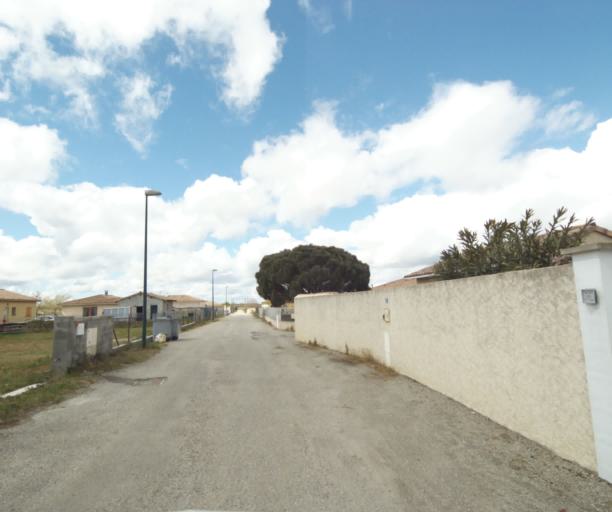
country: FR
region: Midi-Pyrenees
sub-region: Departement de l'Ariege
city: Saverdun
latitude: 43.2386
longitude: 1.5922
